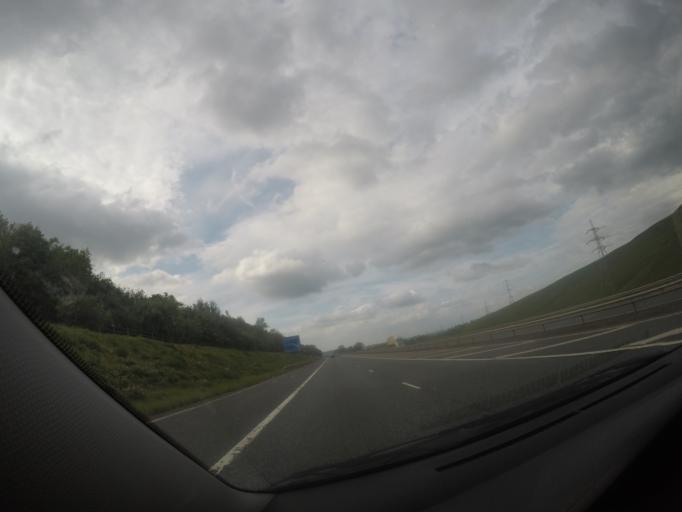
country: GB
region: Scotland
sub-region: South Lanarkshire
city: Douglas
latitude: 55.5611
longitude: -3.8043
